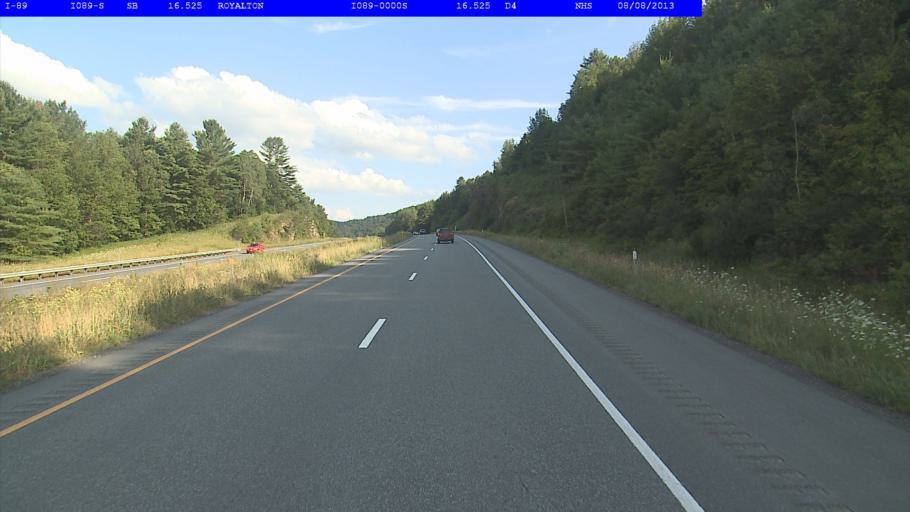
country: US
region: Vermont
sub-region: Windsor County
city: Woodstock
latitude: 43.7957
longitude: -72.5069
